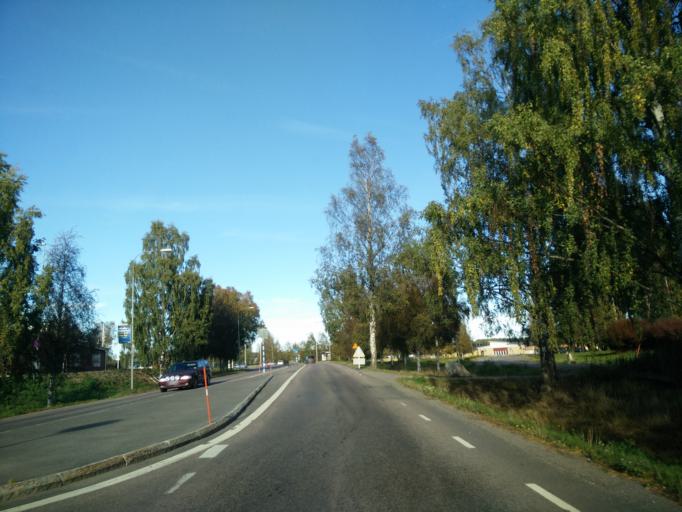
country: SE
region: Gaevleborg
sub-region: Hudiksvalls Kommun
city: Hudiksvall
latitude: 61.7419
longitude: 17.1165
